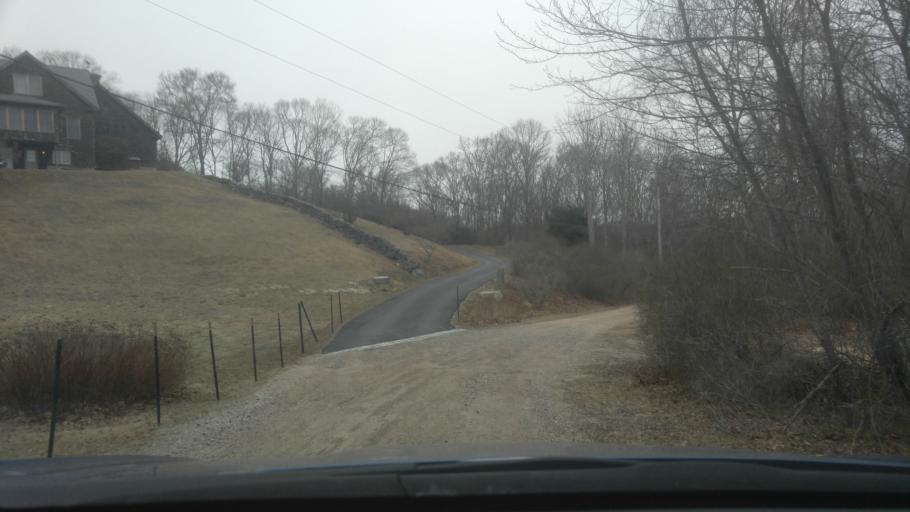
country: US
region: Rhode Island
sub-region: Washington County
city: Wakefield-Peacedale
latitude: 41.4094
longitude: -71.5149
